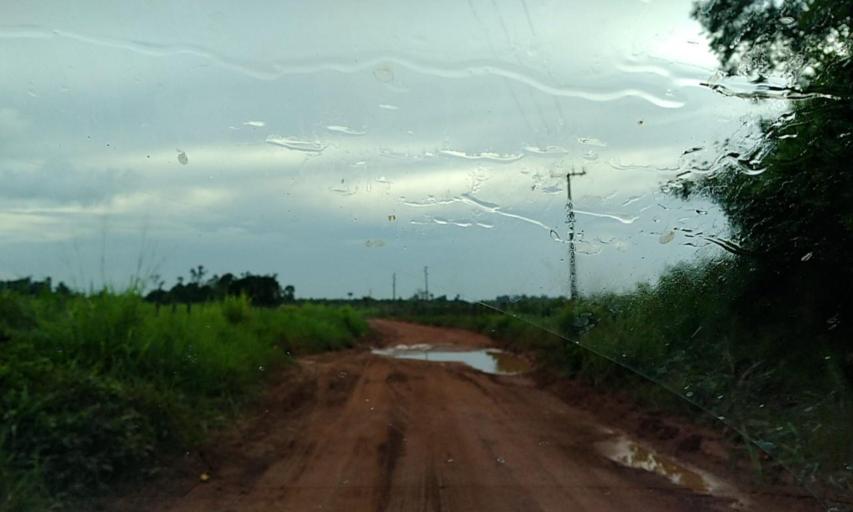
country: BR
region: Para
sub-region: Senador Jose Porfirio
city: Senador Jose Porfirio
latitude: -2.5539
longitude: -51.8695
